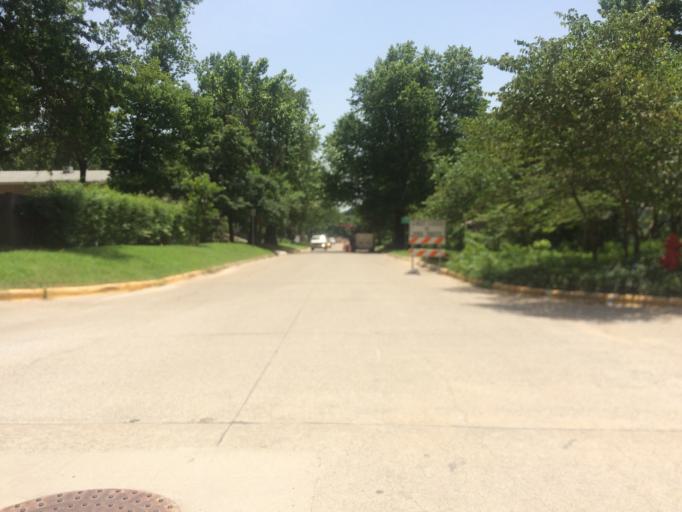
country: US
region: Oklahoma
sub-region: Cleveland County
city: Norman
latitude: 35.2058
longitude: -97.4546
